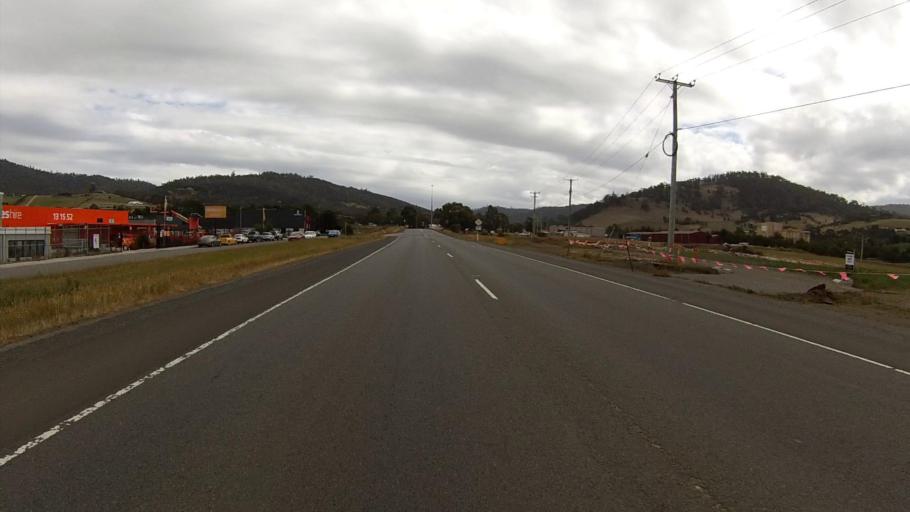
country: AU
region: Tasmania
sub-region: Clarence
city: Cambridge
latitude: -42.8330
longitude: 147.4583
